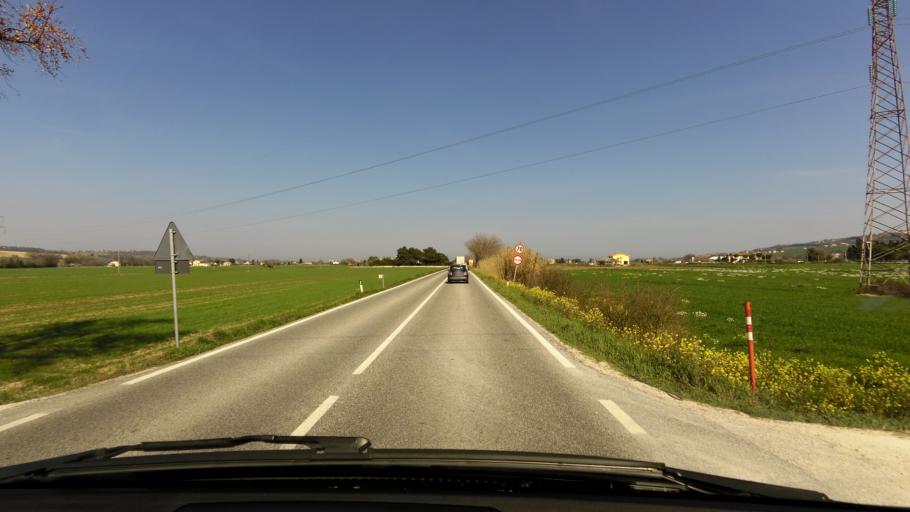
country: IT
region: The Marches
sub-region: Provincia di Macerata
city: Potenza Picena
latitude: 43.3836
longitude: 13.6167
